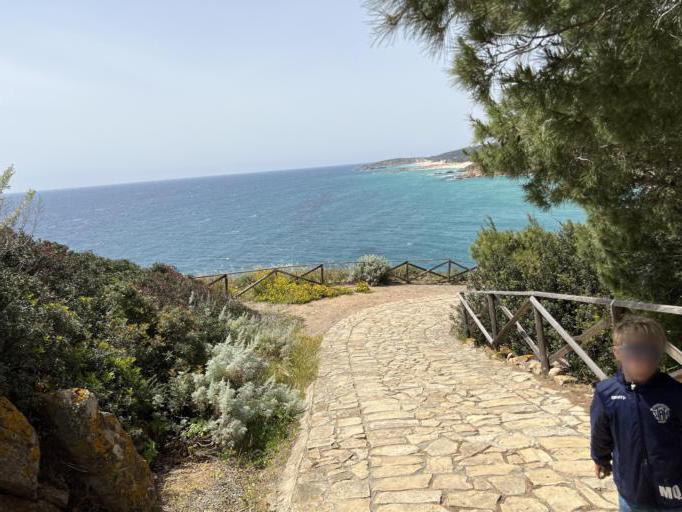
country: IT
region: Sardinia
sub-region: Provincia di Cagliari
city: Domus de Maria
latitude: 38.8953
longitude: 8.8846
